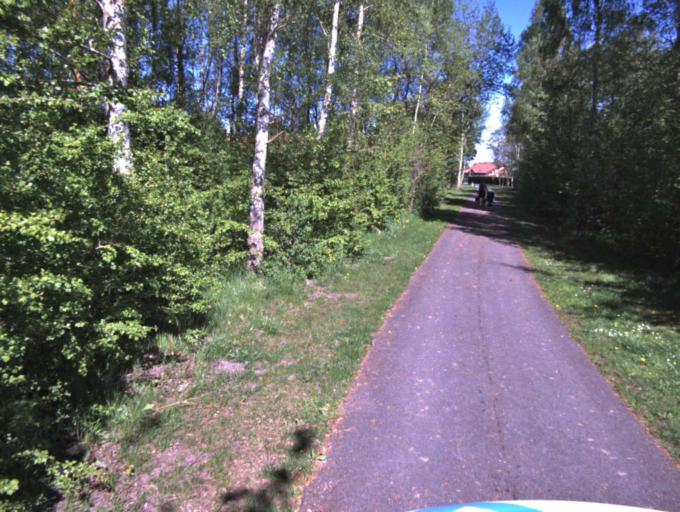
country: SE
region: Skane
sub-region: Kristianstads Kommun
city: Norra Asum
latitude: 56.0013
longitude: 14.1453
